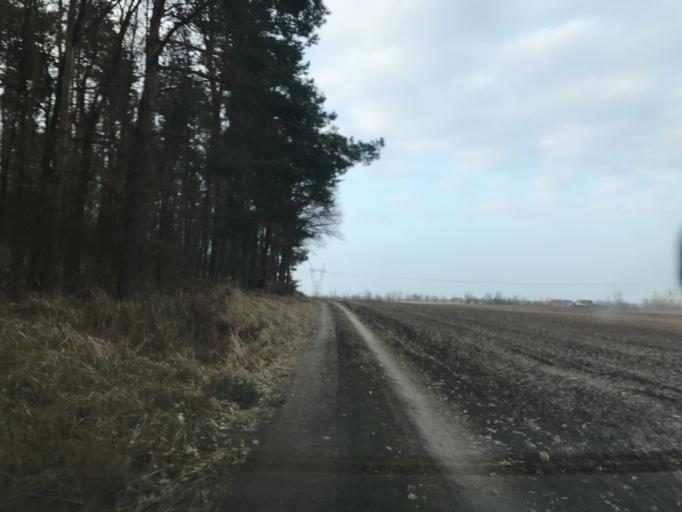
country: PL
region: Kujawsko-Pomorskie
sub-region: Powiat golubsko-dobrzynski
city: Golub-Dobrzyn
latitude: 53.1797
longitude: 18.9995
